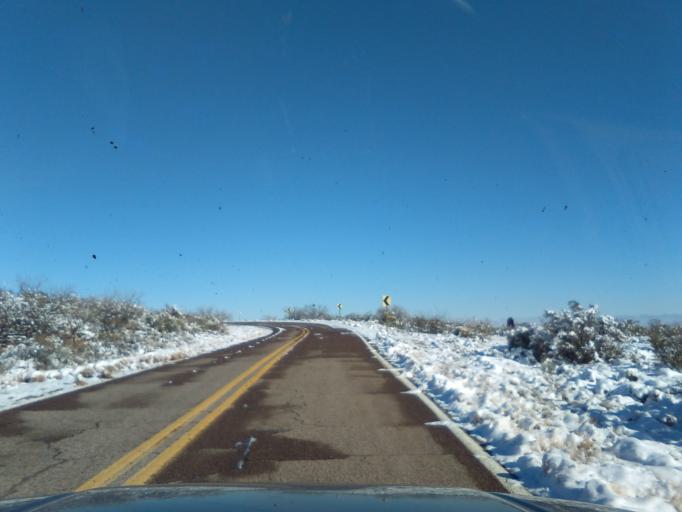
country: US
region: New Mexico
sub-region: Sierra County
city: Elephant Butte
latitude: 33.6195
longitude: -107.1393
